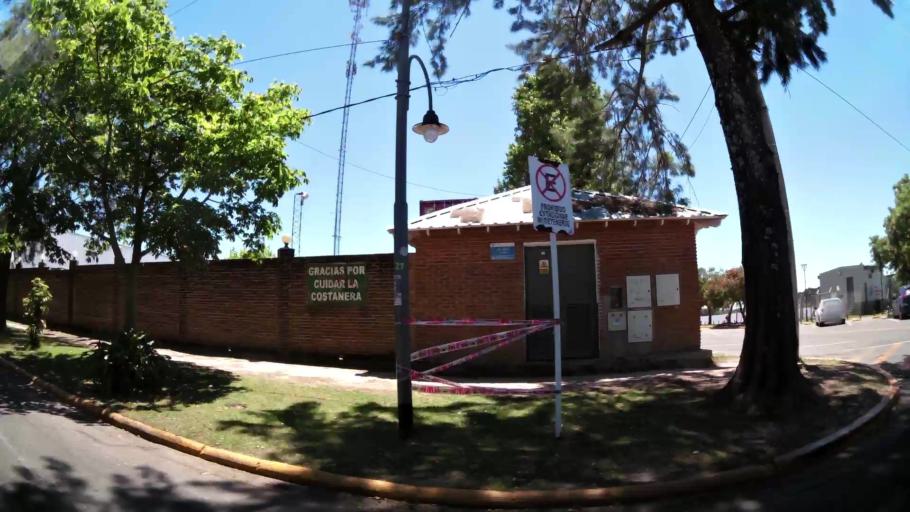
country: AR
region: Buenos Aires
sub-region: Partido de San Isidro
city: San Isidro
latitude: -34.4395
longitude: -58.5366
